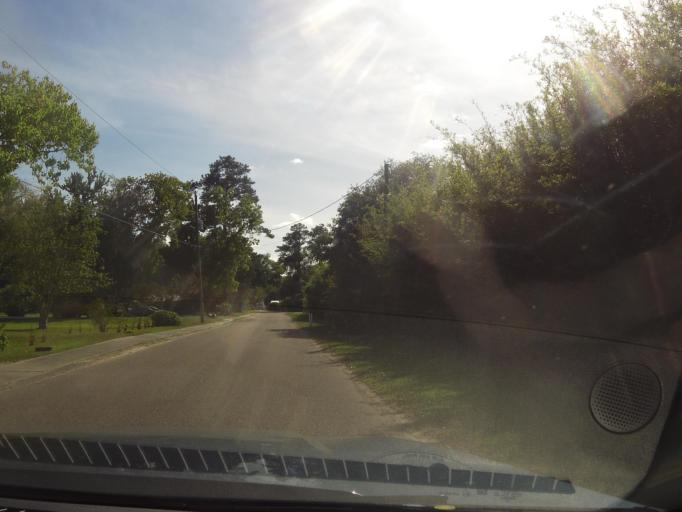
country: US
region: Florida
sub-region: Nassau County
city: Callahan
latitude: 30.5563
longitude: -81.8305
